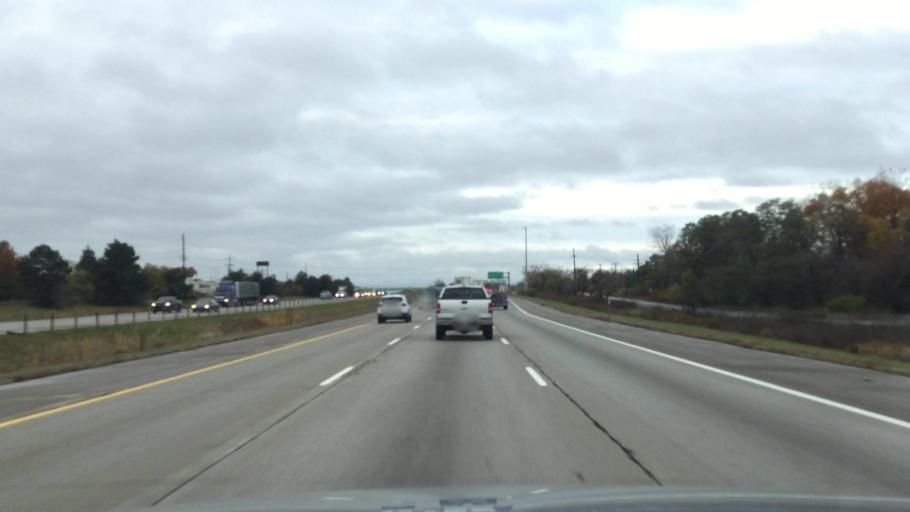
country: US
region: Michigan
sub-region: Wayne County
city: Belleville
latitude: 42.2190
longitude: -83.5356
